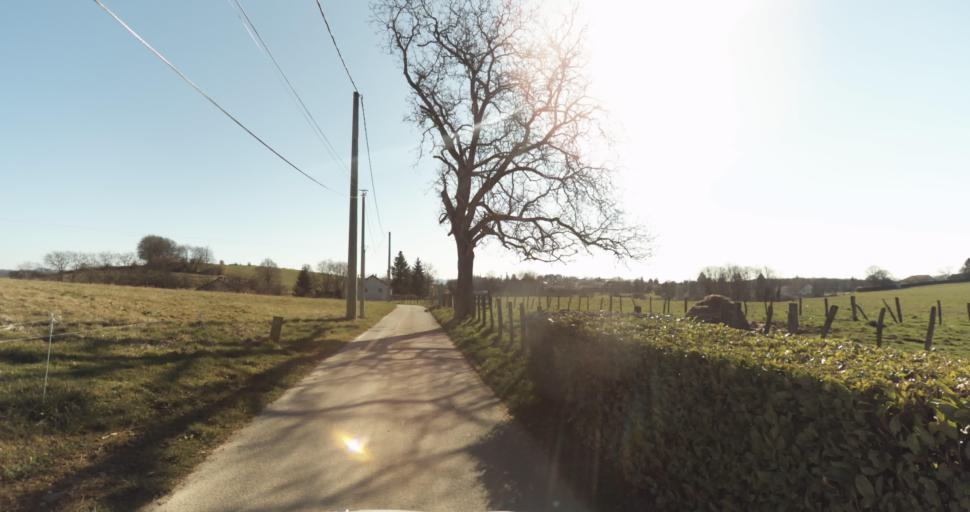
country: FR
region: Franche-Comte
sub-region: Departement du Jura
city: Montmorot
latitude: 46.6982
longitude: 5.5176
